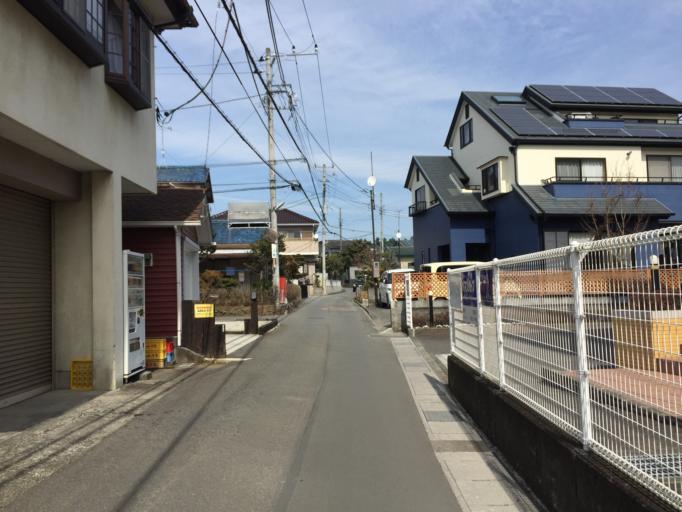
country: JP
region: Shizuoka
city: Mishima
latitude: 35.1668
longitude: 138.9138
